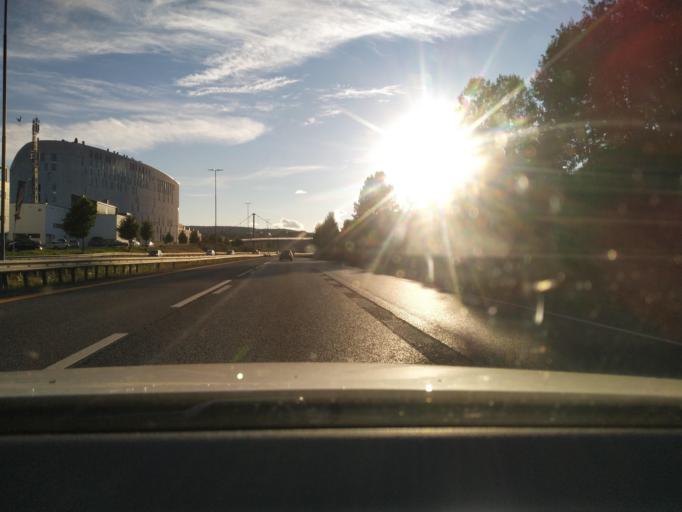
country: NO
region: Akershus
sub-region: Lorenskog
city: Kjenn
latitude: 59.9296
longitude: 10.9654
